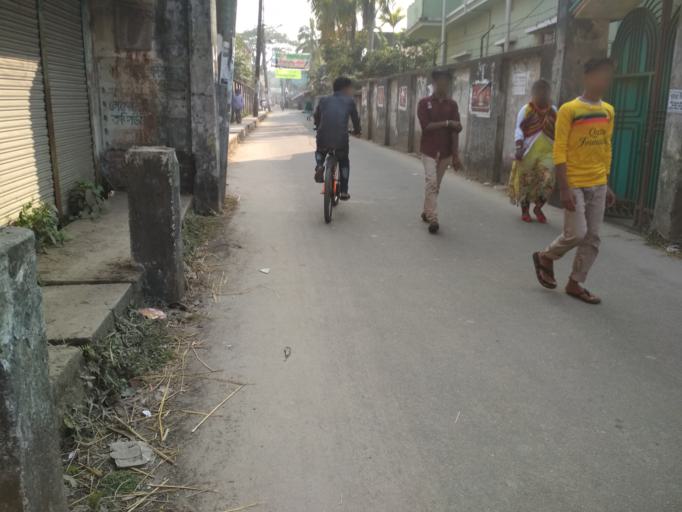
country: BD
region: Chittagong
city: Lakshmipur
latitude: 22.9338
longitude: 90.8262
